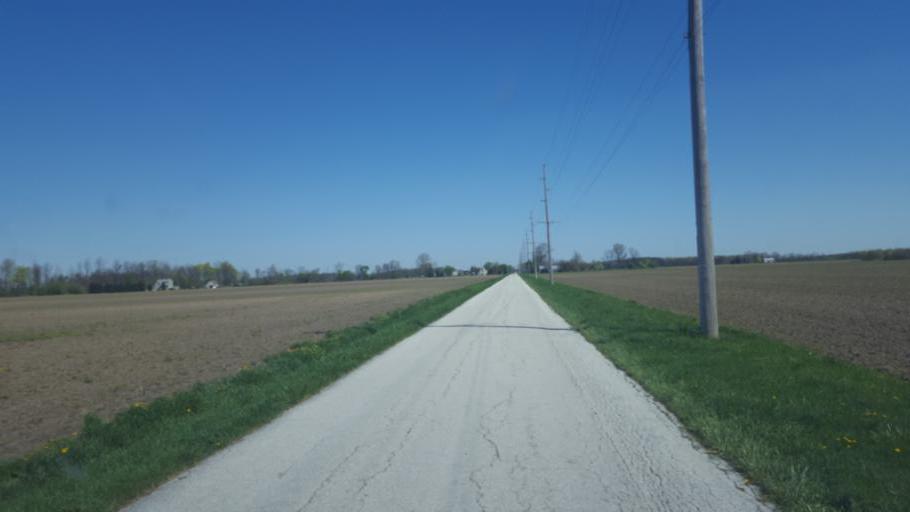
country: US
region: Ohio
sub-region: Sandusky County
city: Ballville
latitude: 41.2340
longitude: -83.1871
